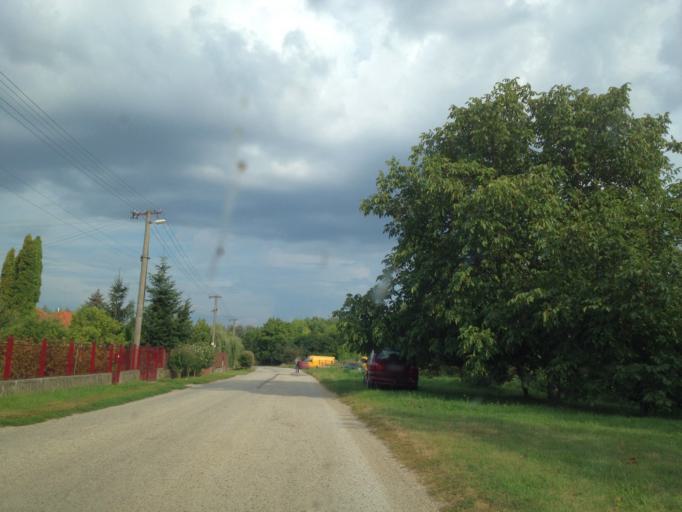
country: SK
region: Nitriansky
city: Svodin
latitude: 47.8965
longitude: 18.4081
